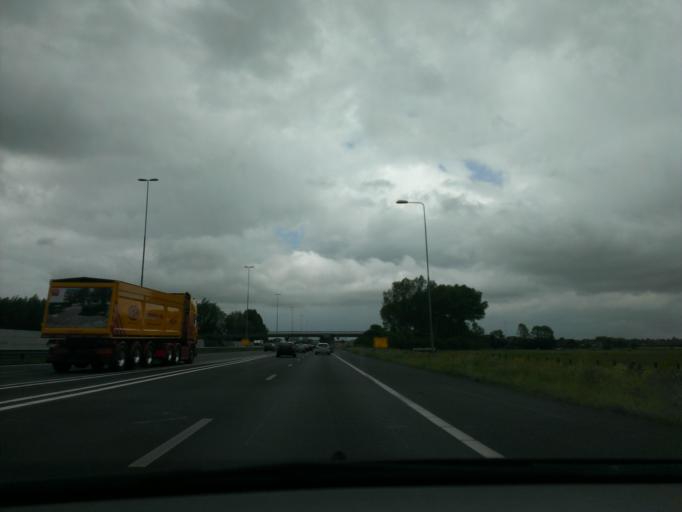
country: NL
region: Gelderland
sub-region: Gemeente Overbetuwe
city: Andelst
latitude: 51.8641
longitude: 5.7189
